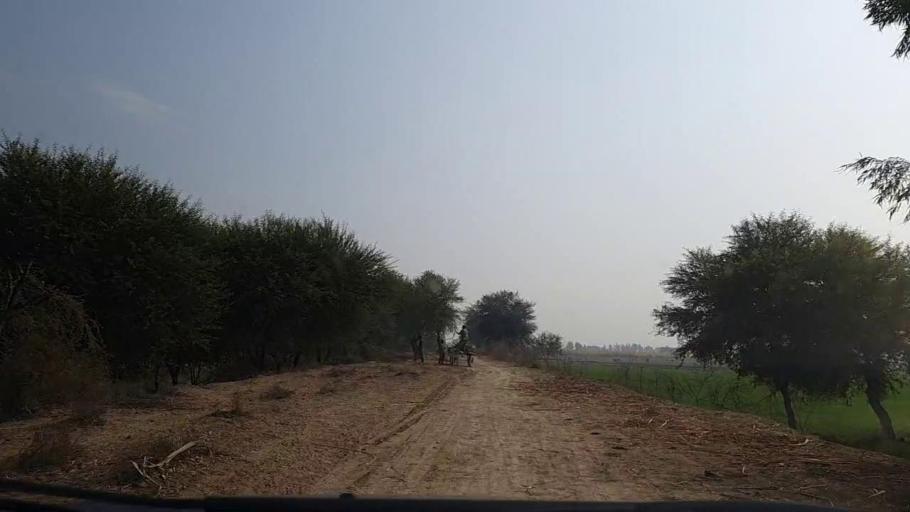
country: PK
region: Sindh
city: Sanghar
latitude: 26.0447
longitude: 68.9903
